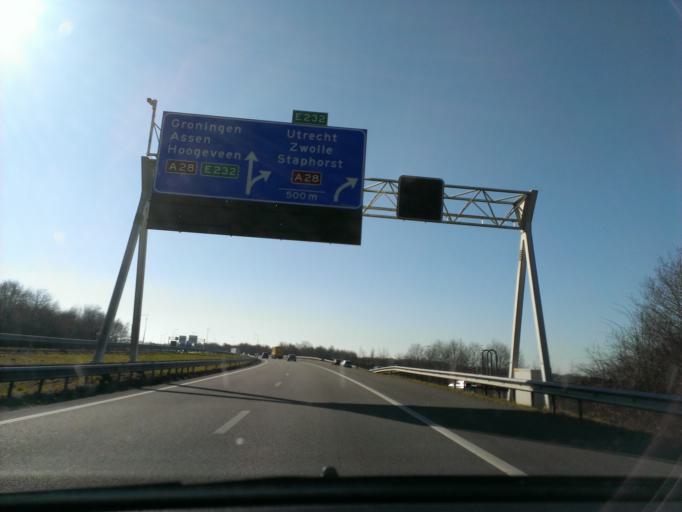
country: NL
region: Drenthe
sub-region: Gemeente Meppel
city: Meppel
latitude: 52.6768
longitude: 6.1925
